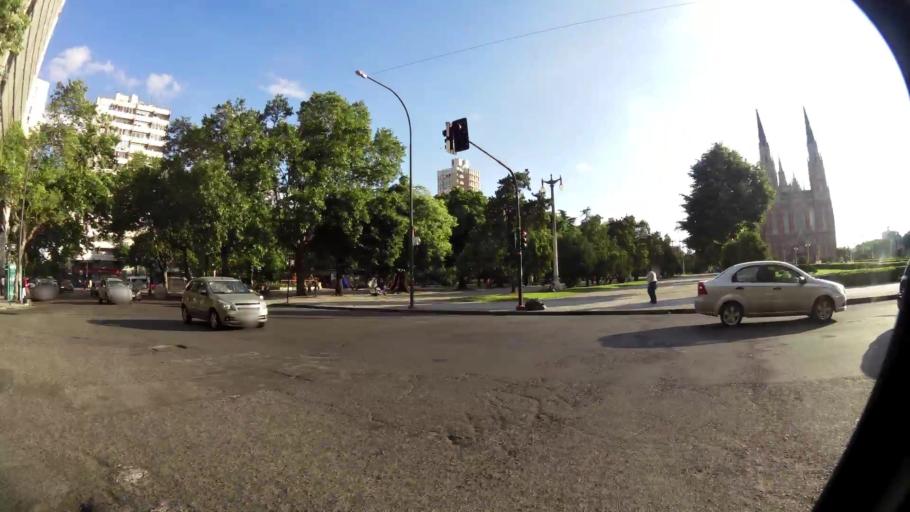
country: AR
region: Buenos Aires
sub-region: Partido de La Plata
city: La Plata
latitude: -34.9208
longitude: -57.9530
